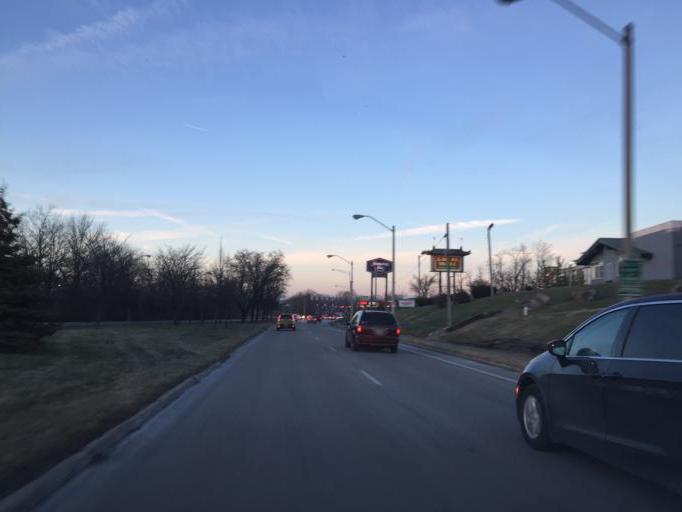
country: US
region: Indiana
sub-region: Monroe County
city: Bloomington
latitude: 39.1837
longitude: -86.5343
